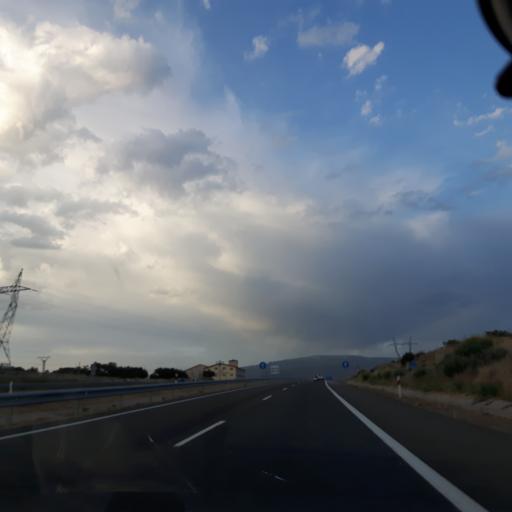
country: ES
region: Castille and Leon
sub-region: Provincia de Salamanca
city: Fuentes de Bejar
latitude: 40.4972
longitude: -5.6758
